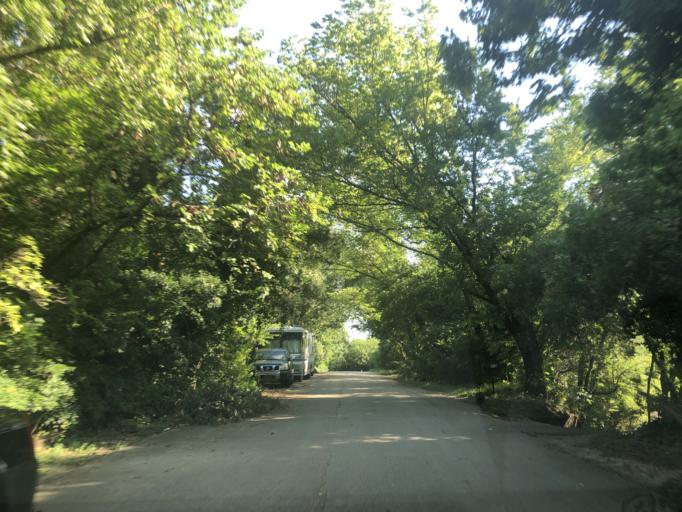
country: US
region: Texas
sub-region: Dallas County
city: Duncanville
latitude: 32.6653
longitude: -96.9233
